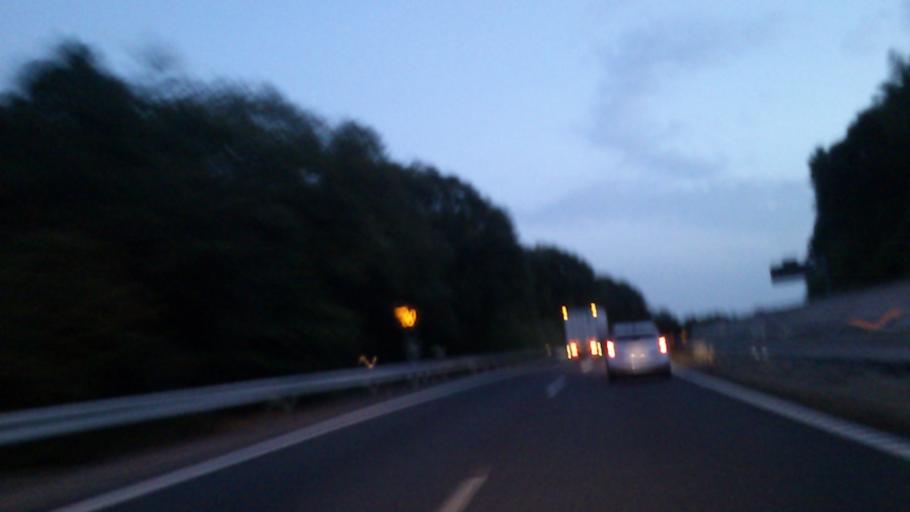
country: JP
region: Aichi
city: Kasugai
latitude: 35.3256
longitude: 137.0236
